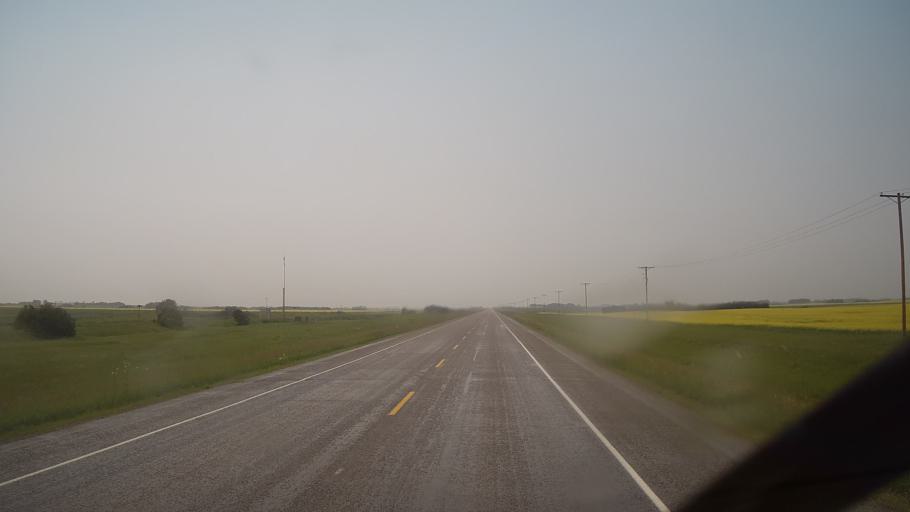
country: CA
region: Saskatchewan
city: Biggar
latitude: 52.1513
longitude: -108.2346
